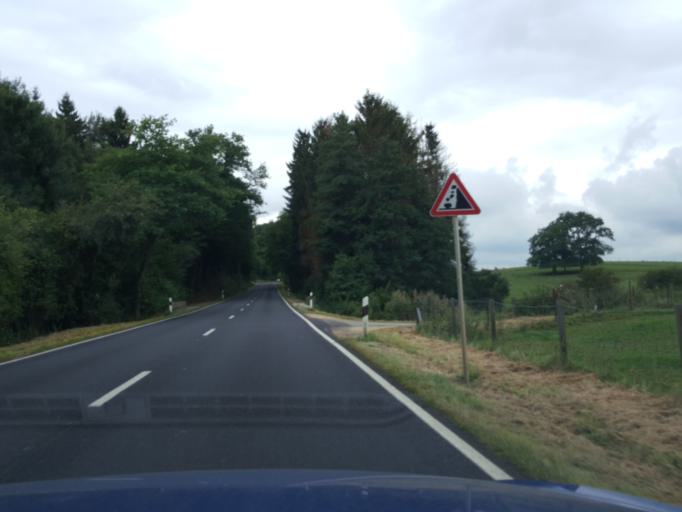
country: LU
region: Luxembourg
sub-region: Canton de Capellen
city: Mamer
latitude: 49.6487
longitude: 6.0265
